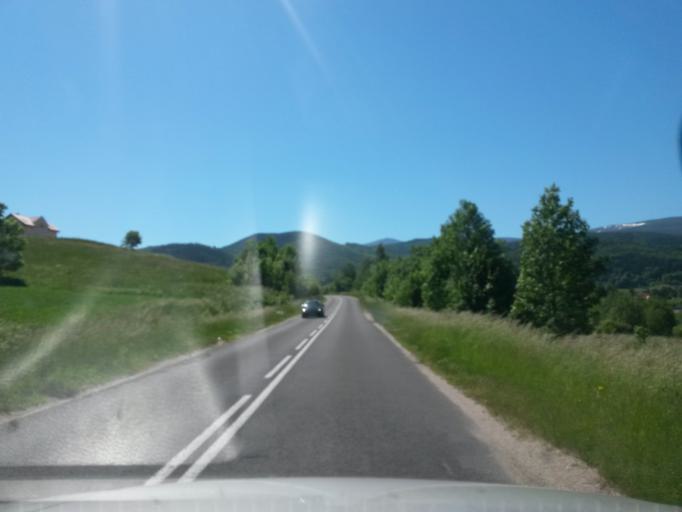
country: PL
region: Lower Silesian Voivodeship
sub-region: Powiat jeleniogorski
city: Sosnowka
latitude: 50.8297
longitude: 15.7214
